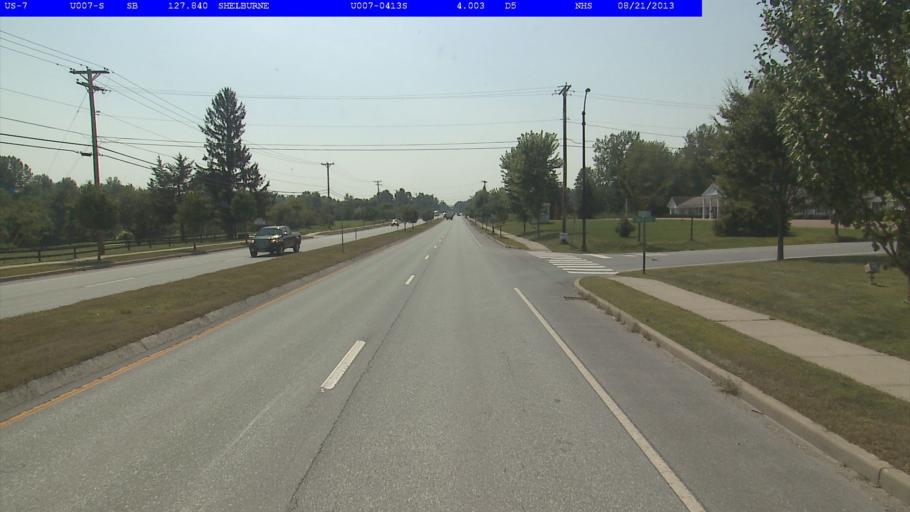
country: US
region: Vermont
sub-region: Chittenden County
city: Burlington
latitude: 44.3995
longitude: -73.2189
